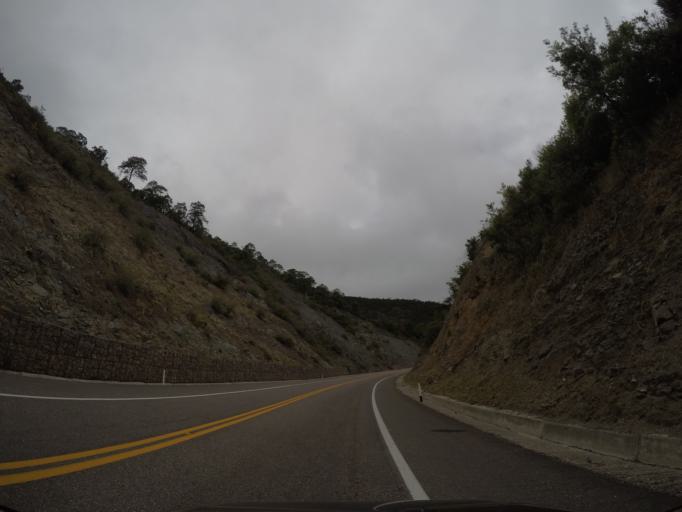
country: MX
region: Oaxaca
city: San Lorenzo Albarradas
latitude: 16.9361
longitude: -96.2728
